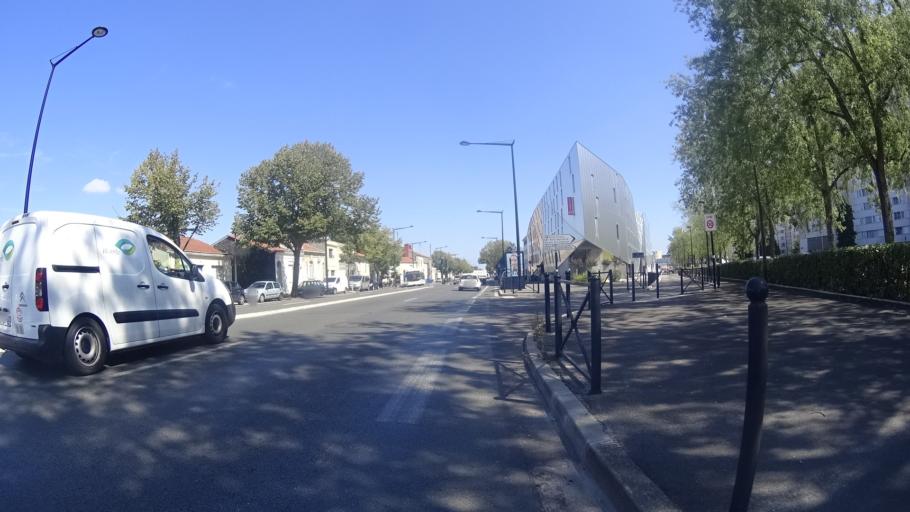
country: FR
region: Aquitaine
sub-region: Departement de la Gironde
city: Le Bouscat
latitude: 44.8632
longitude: -0.5826
